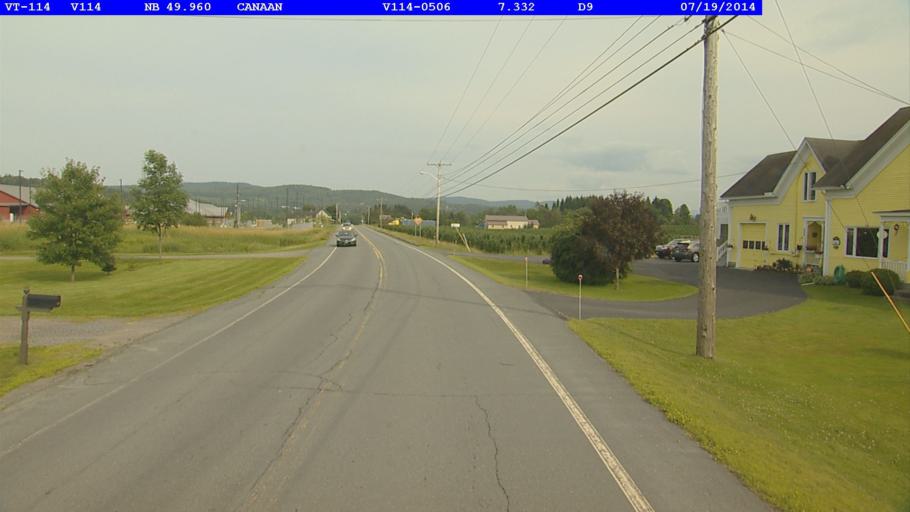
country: US
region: New Hampshire
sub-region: Coos County
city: Colebrook
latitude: 45.0034
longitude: -71.5524
